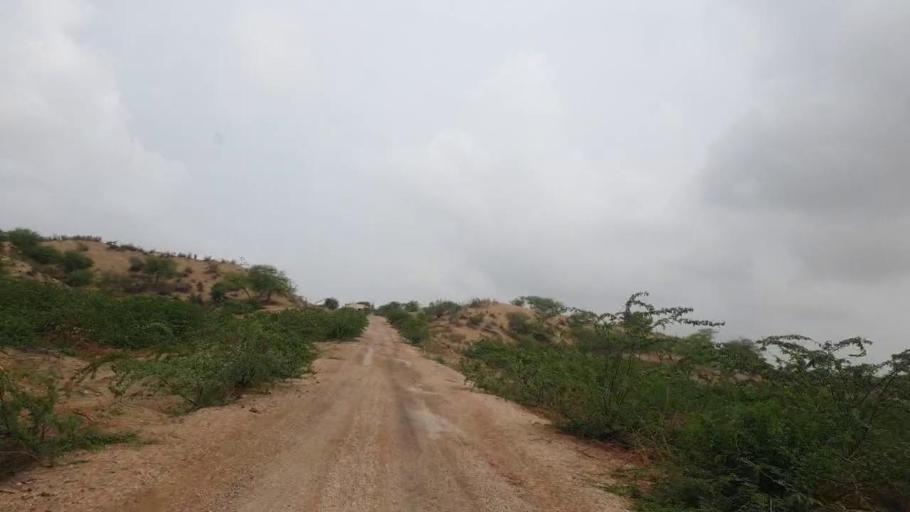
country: PK
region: Sindh
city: Diplo
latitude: 24.5571
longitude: 69.4555
